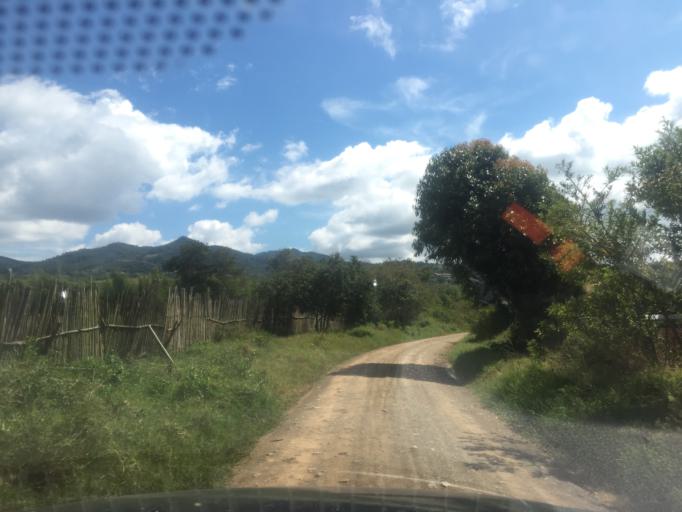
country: CO
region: Valle del Cauca
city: Yumbo
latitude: 3.6673
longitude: -76.5596
